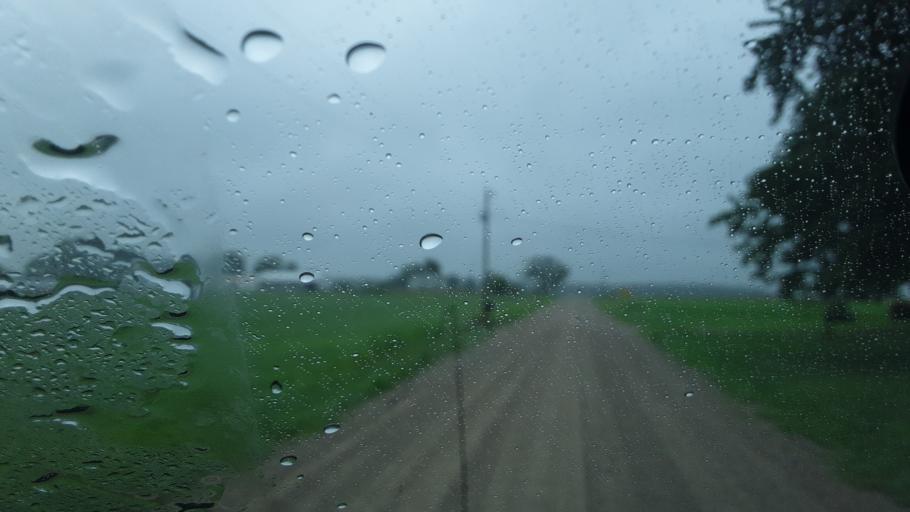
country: US
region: Indiana
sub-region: Adams County
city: Berne
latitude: 40.6349
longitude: -84.9946
